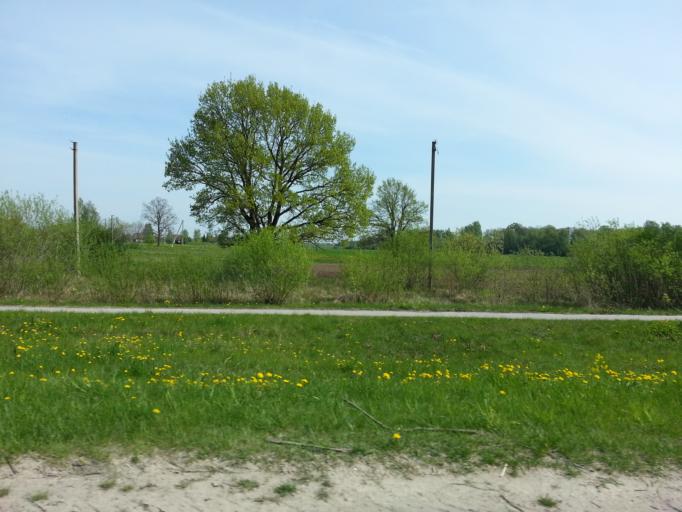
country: LT
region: Panevezys
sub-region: Panevezys City
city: Panevezys
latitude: 55.7749
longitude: 24.2923
